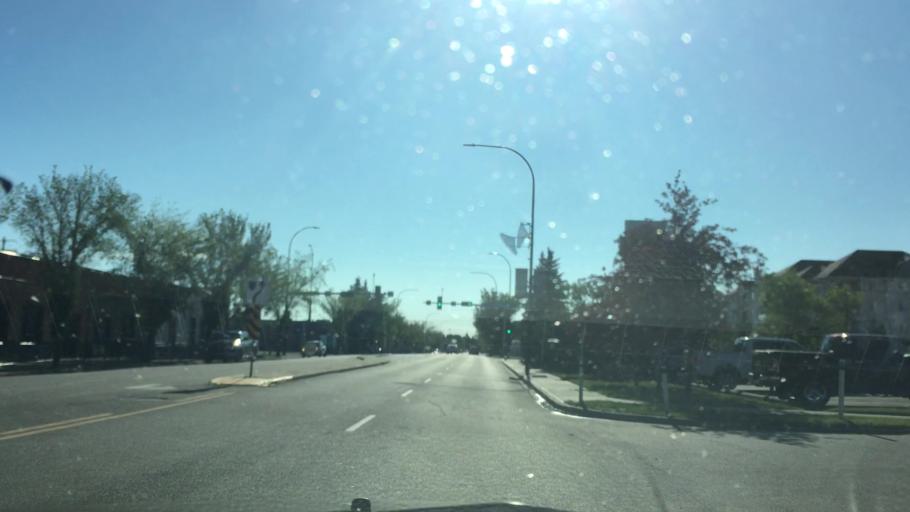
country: CA
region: Alberta
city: Leduc
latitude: 53.2647
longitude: -113.5592
